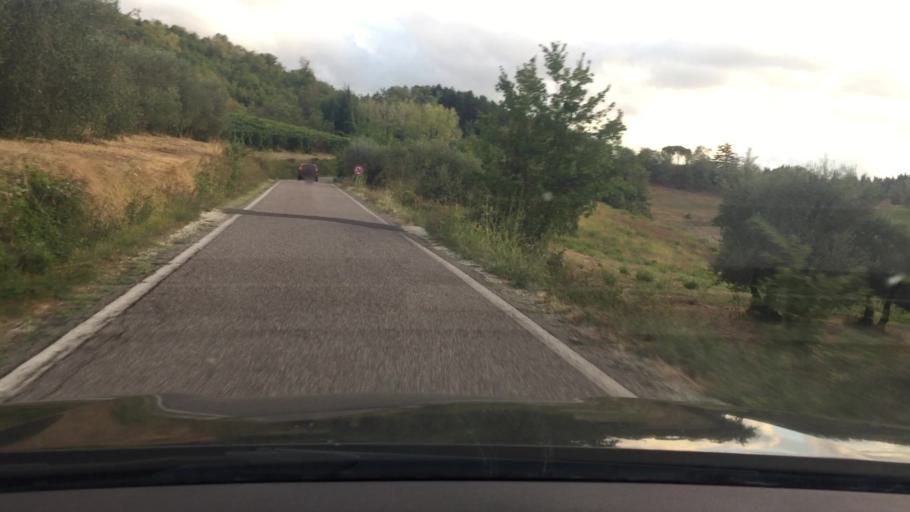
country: IT
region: Emilia-Romagna
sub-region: Provincia di Ravenna
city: Brisighella
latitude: 44.2052
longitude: 11.7767
